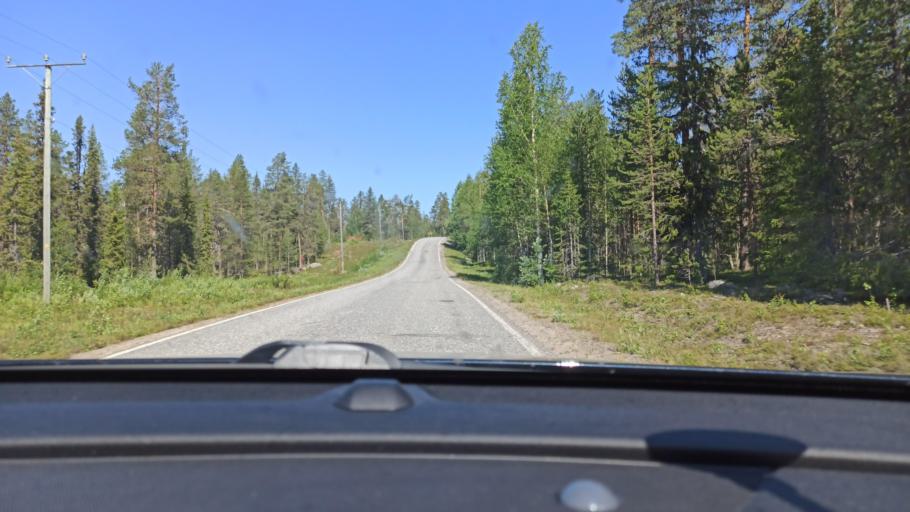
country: FI
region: Lapland
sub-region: Tunturi-Lappi
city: Kolari
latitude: 67.6354
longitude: 24.1584
